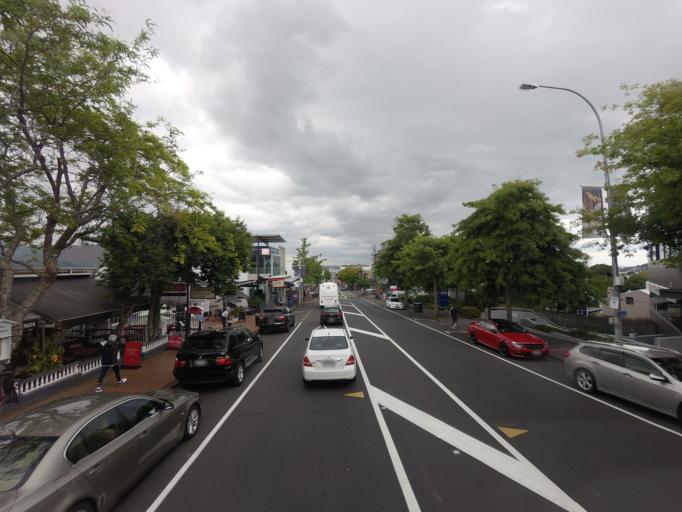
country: NZ
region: Auckland
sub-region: Auckland
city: Auckland
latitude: -36.8571
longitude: 174.7811
